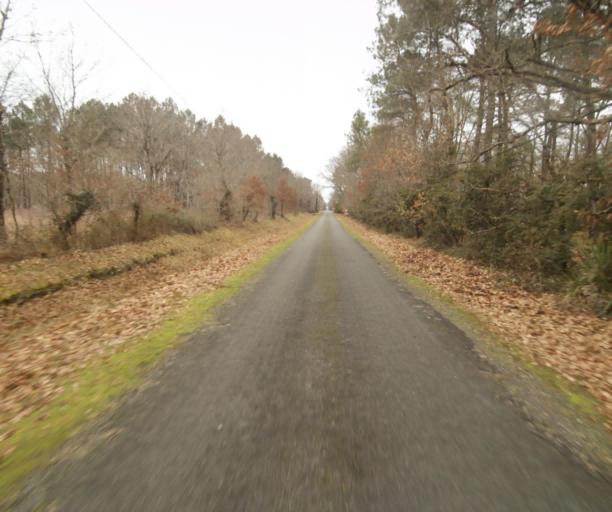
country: FR
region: Aquitaine
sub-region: Departement des Landes
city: Gabarret
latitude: 44.0446
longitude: -0.0843
